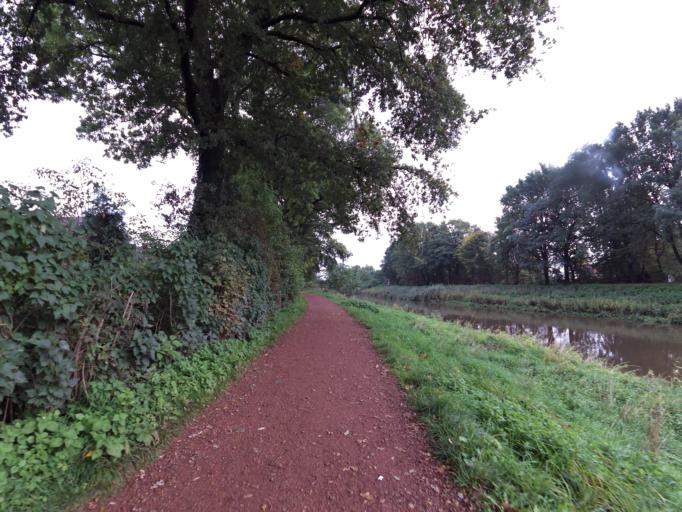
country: DE
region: North Rhine-Westphalia
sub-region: Regierungsbezirk Dusseldorf
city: Bocholt
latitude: 51.8406
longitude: 6.5864
